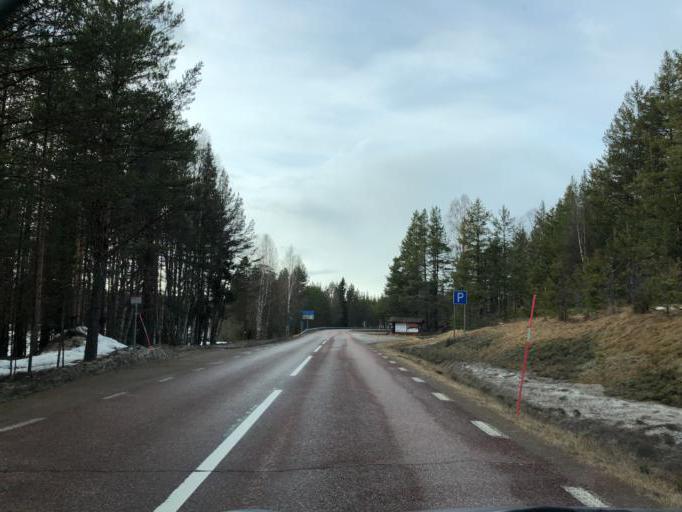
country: NO
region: Hedmark
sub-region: Trysil
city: Innbygda
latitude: 61.7948
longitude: 12.9222
